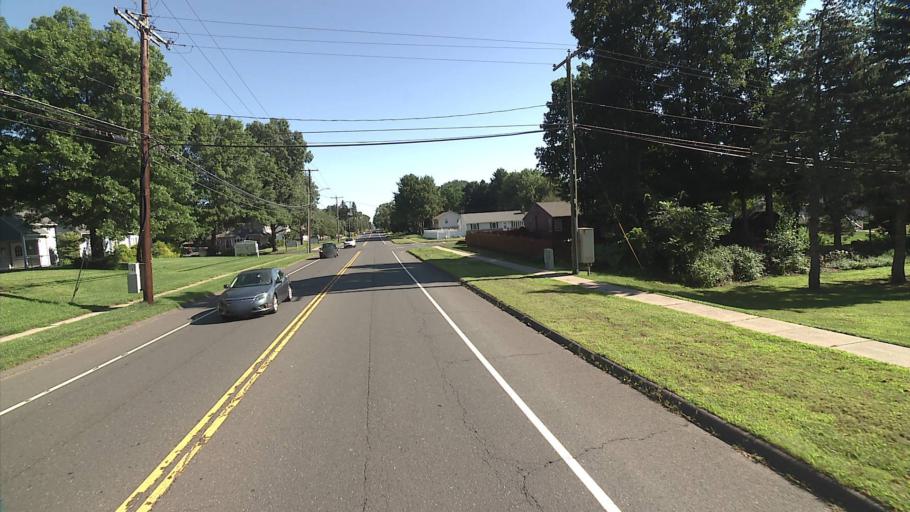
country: US
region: Connecticut
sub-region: New Haven County
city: Cheshire Village
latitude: 41.5115
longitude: -72.8991
